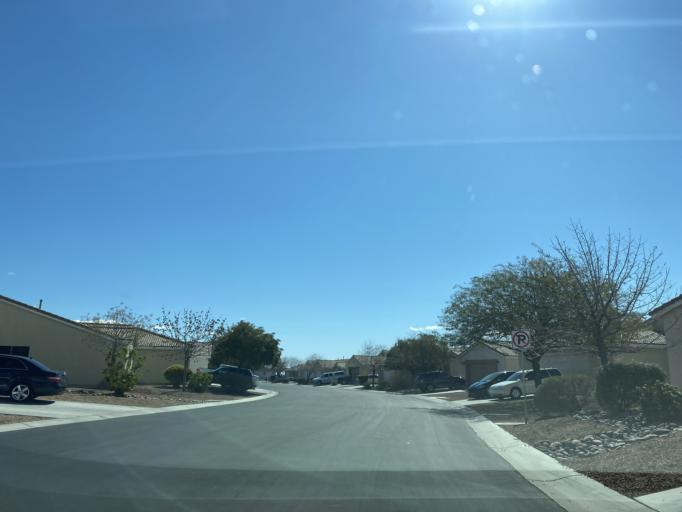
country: US
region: Nevada
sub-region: Clark County
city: North Las Vegas
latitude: 36.3300
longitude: -115.2675
